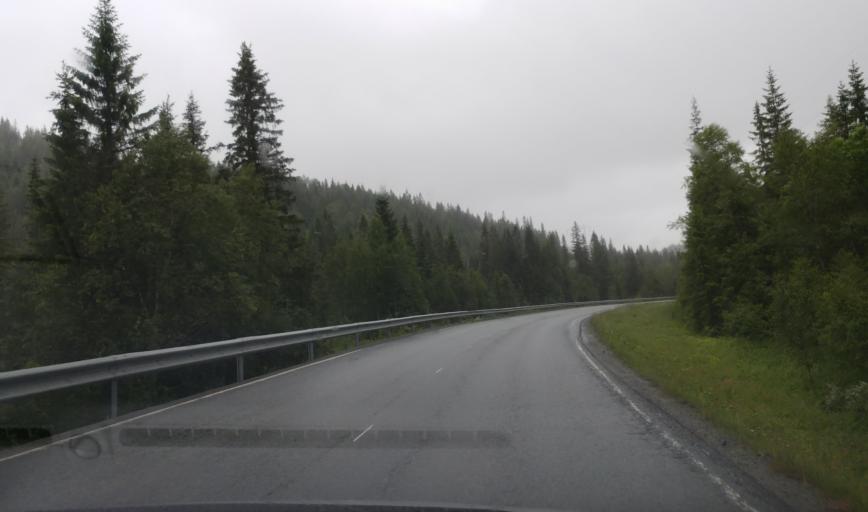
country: NO
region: Sor-Trondelag
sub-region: Selbu
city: Mebonden
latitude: 63.3369
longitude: 11.0926
